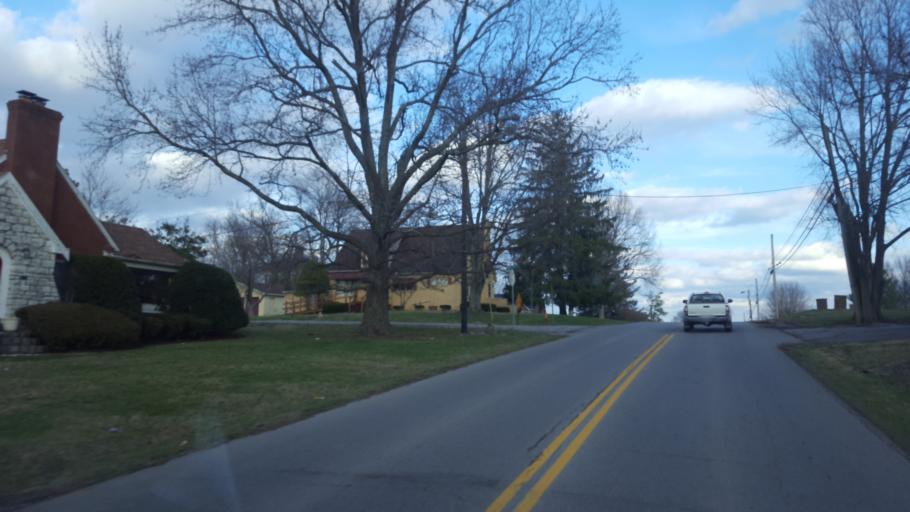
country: US
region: Kentucky
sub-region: Fleming County
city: Flemingsburg
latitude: 38.4200
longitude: -83.7428
